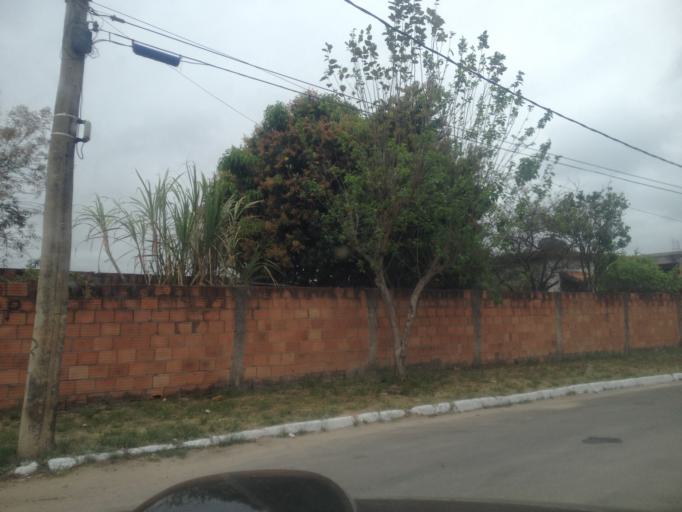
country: BR
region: Rio de Janeiro
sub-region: Porto Real
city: Porto Real
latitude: -22.4139
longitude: -44.3067
